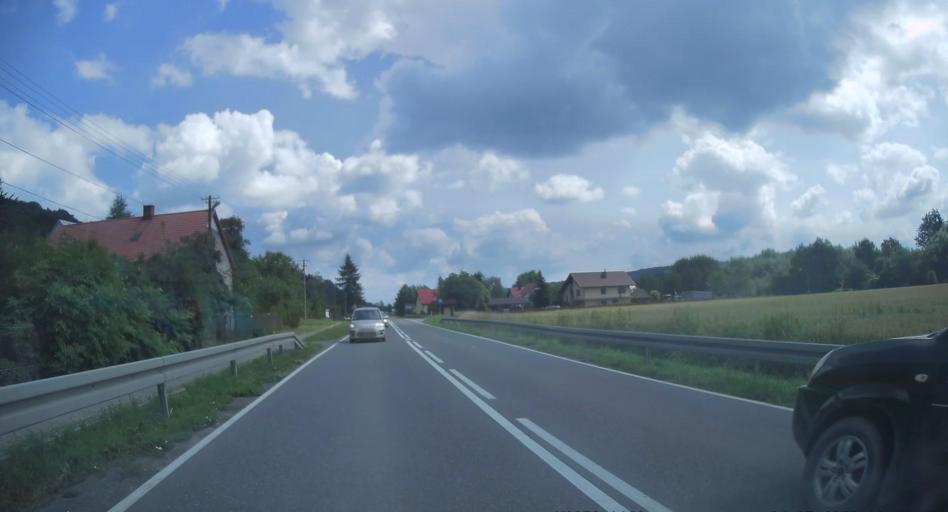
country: PL
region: Lesser Poland Voivodeship
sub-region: Powiat tarnowski
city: Wielka Wies
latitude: 49.9171
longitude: 20.8211
